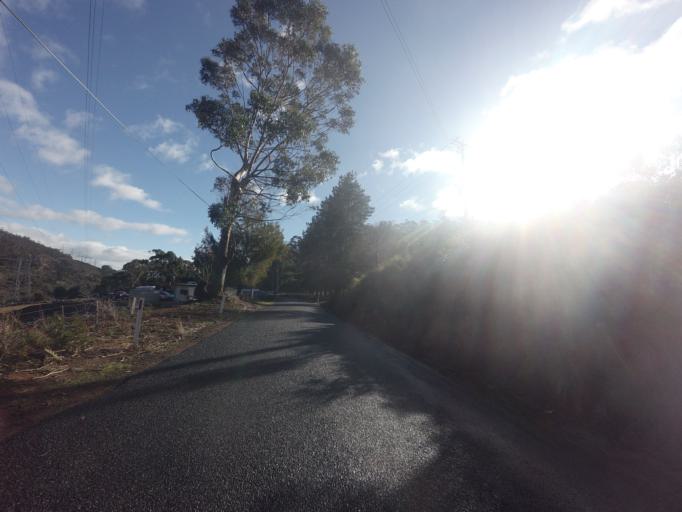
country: AU
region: Tasmania
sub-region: Glenorchy
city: Berriedale
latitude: -42.8130
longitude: 147.1744
